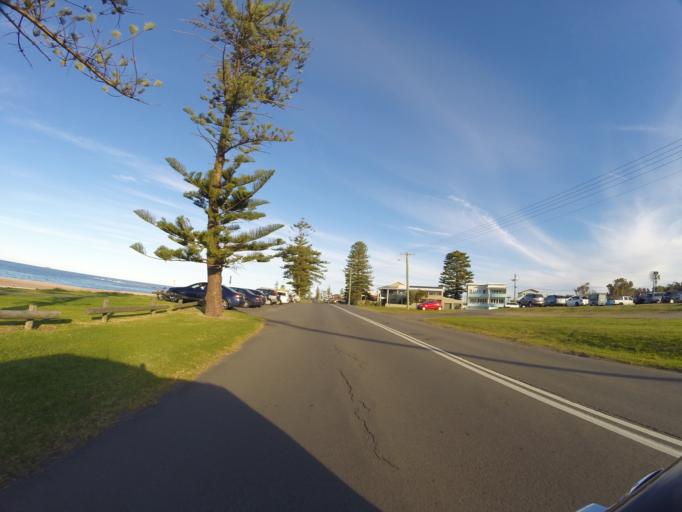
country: AU
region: New South Wales
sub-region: Wollongong
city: Bulli
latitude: -34.3358
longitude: 150.9239
